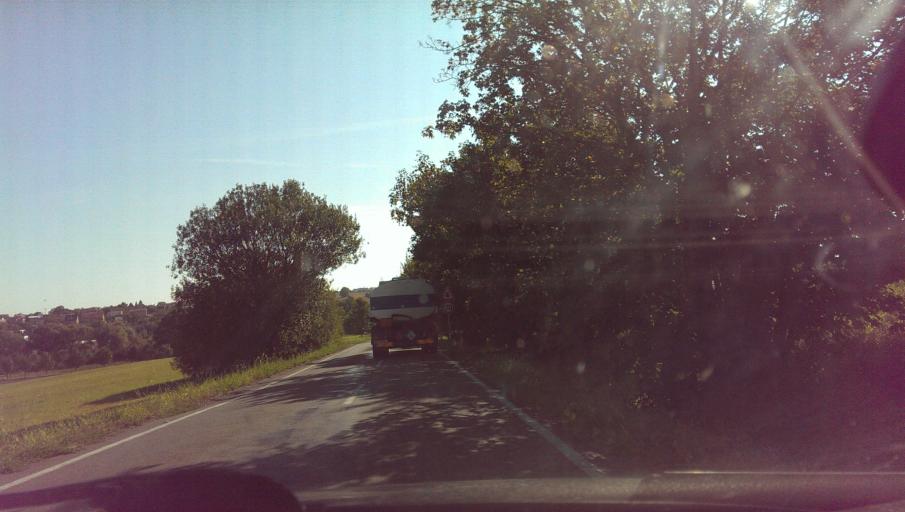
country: CZ
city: Brusperk
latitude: 49.6907
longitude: 18.2201
